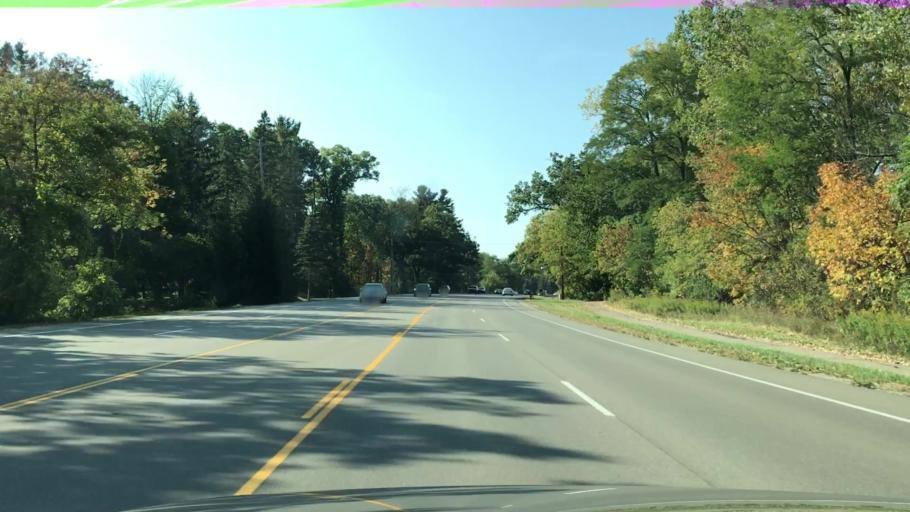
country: US
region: Michigan
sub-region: Kent County
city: Forest Hills
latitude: 42.9292
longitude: -85.5189
